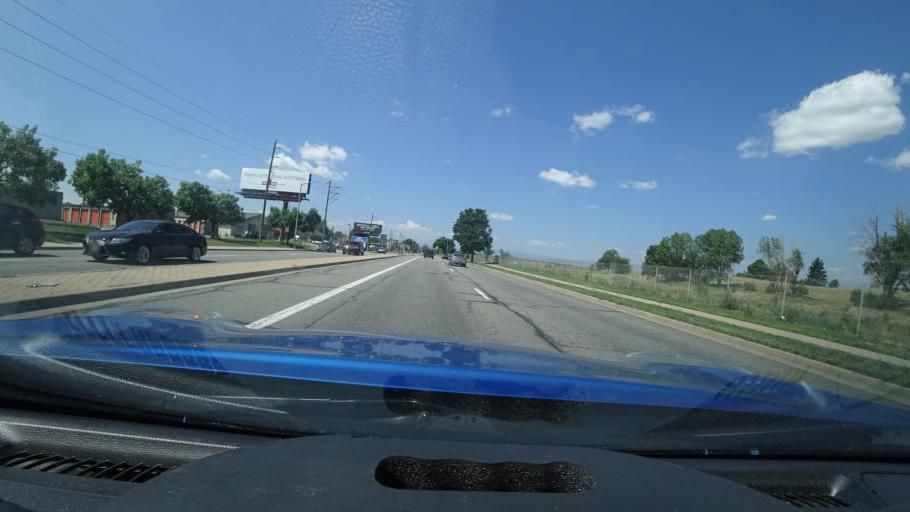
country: US
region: Colorado
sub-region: Adams County
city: Aurora
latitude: 39.7097
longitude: -104.8726
